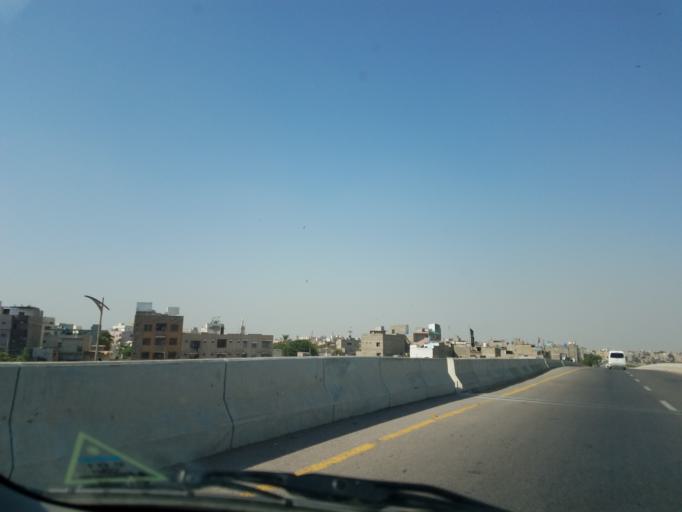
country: PK
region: Sindh
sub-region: Karachi District
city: Karachi
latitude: 24.9167
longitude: 67.0784
